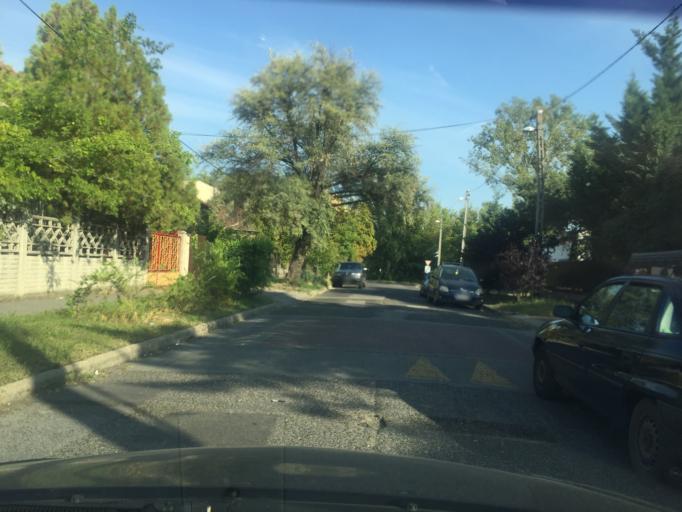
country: HU
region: Budapest
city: Budapest XV. keruelet
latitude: 47.5750
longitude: 19.1026
